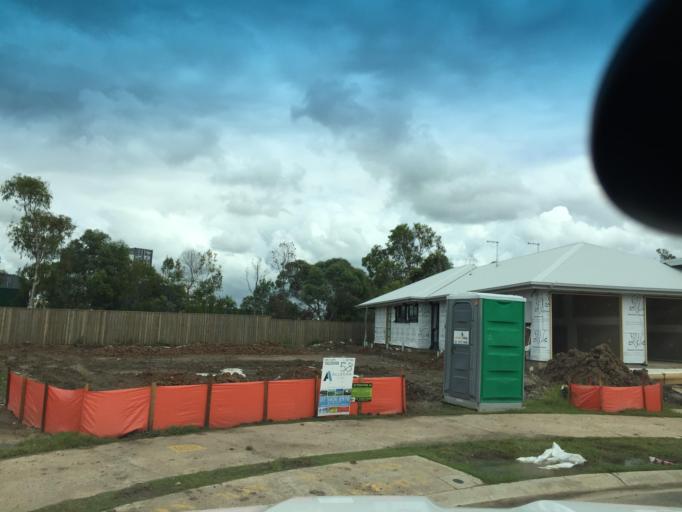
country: AU
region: Queensland
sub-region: Moreton Bay
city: Burpengary
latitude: -27.1614
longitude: 152.9832
